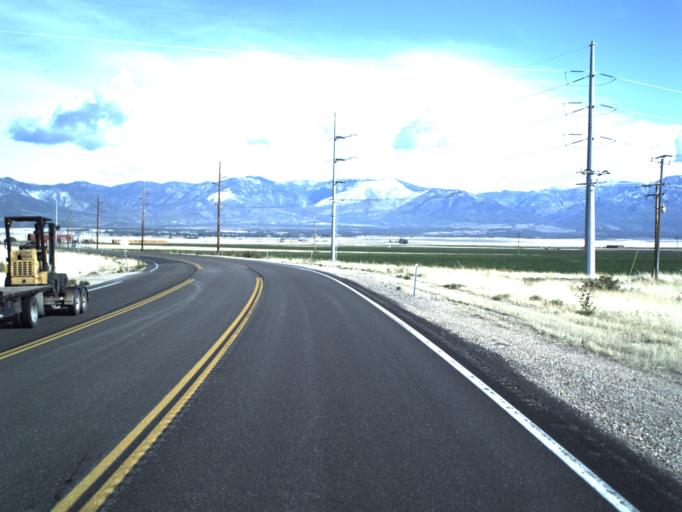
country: US
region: Utah
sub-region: Millard County
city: Fillmore
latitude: 39.1184
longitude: -112.3538
